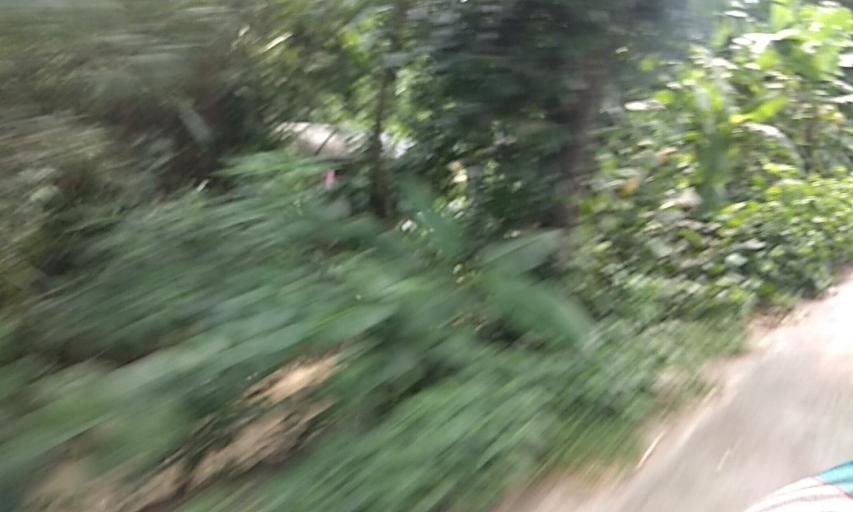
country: BD
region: Dhaka
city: Dohar
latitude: 23.4742
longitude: 90.0387
